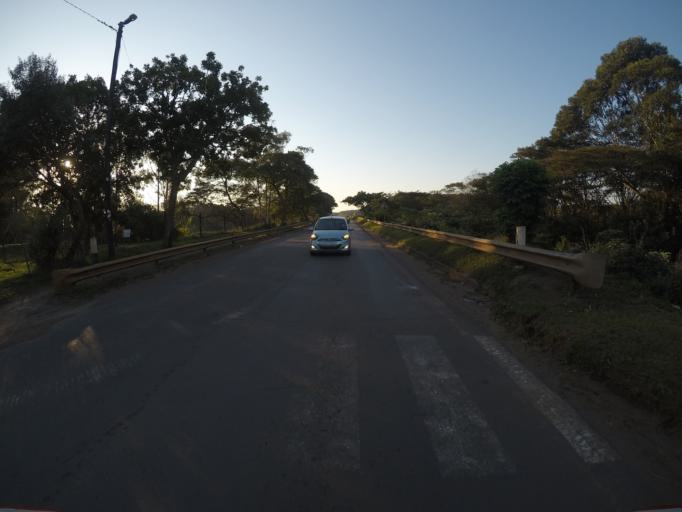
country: ZA
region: KwaZulu-Natal
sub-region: uThungulu District Municipality
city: KwaMbonambi
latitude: -28.6859
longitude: 32.1423
